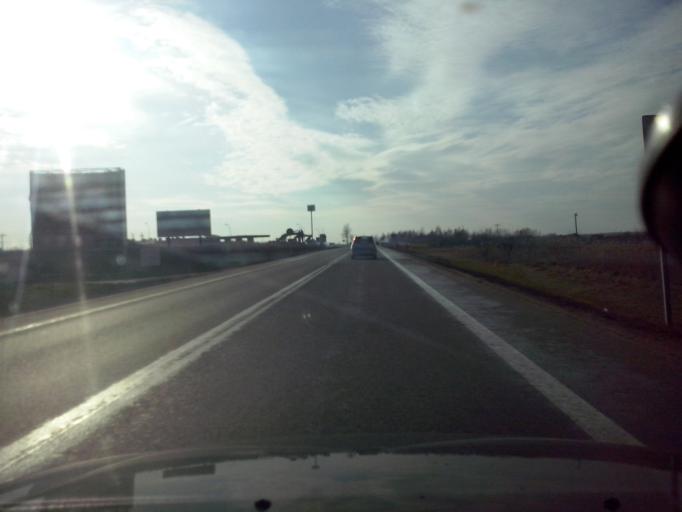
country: PL
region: Subcarpathian Voivodeship
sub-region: Powiat rzeszowski
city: Wolka Podlesna
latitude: 50.1675
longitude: 22.0855
